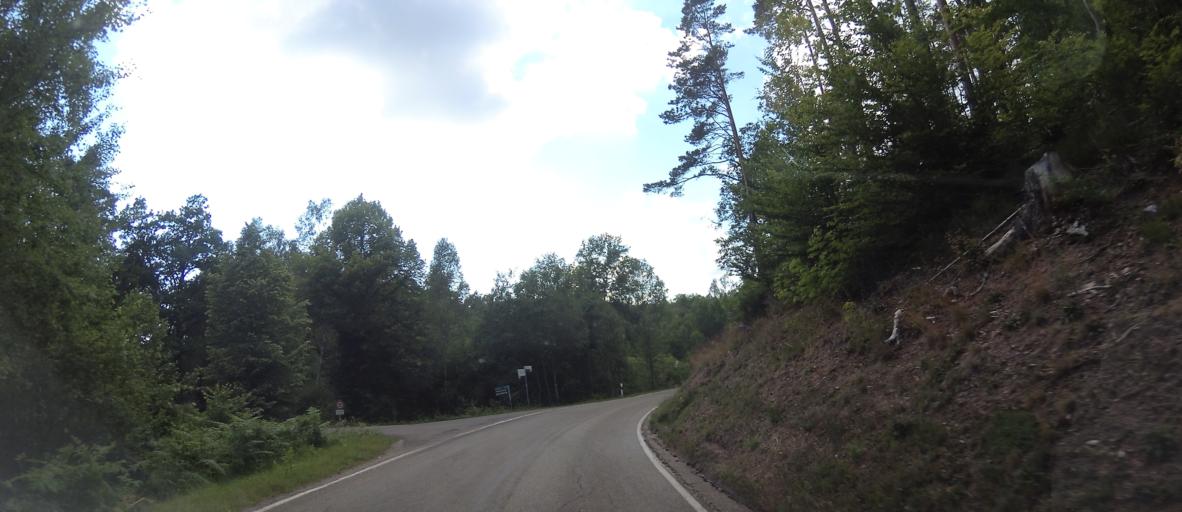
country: DE
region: Rheinland-Pfalz
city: Eppenbrunn
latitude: 49.1077
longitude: 7.5688
